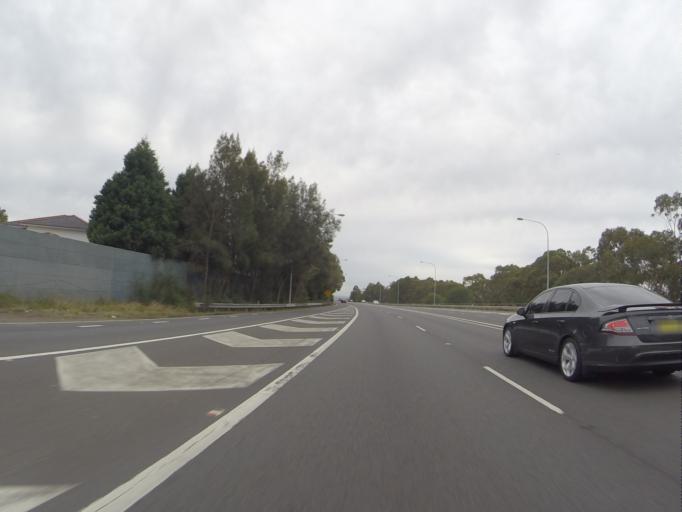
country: AU
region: New South Wales
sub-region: Hurstville
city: Lugarno
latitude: -33.9945
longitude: 151.0266
